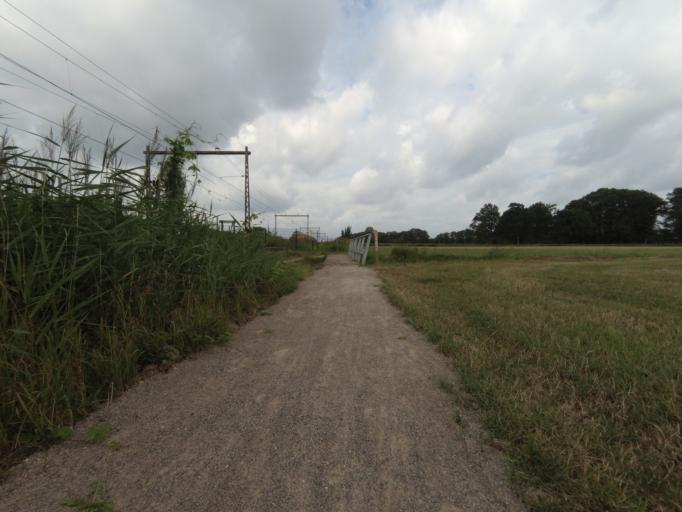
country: NL
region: Overijssel
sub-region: Gemeente Borne
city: Borne
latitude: 52.3169
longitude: 6.7162
